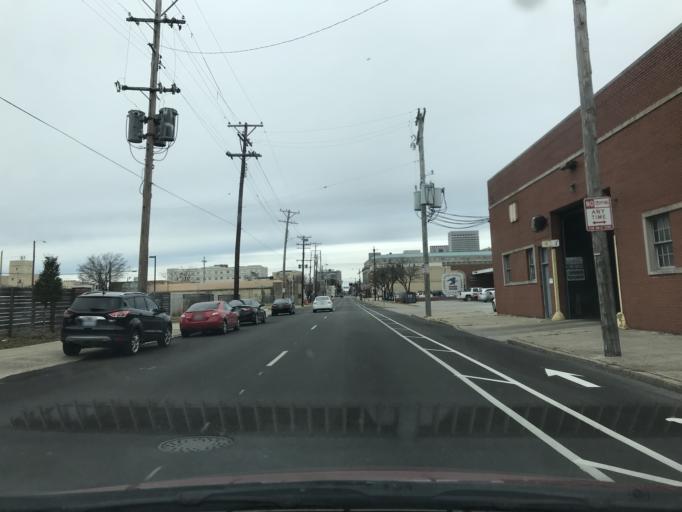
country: US
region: Kentucky
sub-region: Jefferson County
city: Louisville
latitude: 38.2432
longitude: -85.7640
